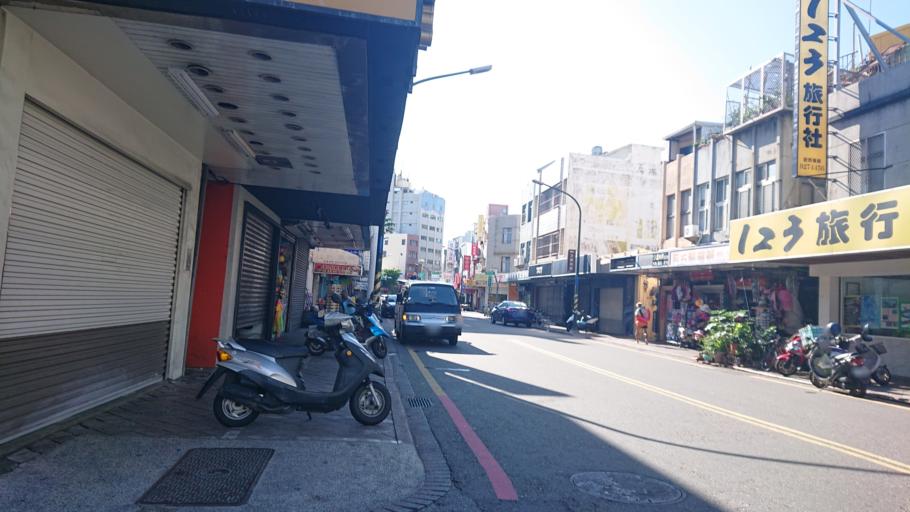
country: TW
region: Taiwan
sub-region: Penghu
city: Ma-kung
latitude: 23.5676
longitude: 119.5667
